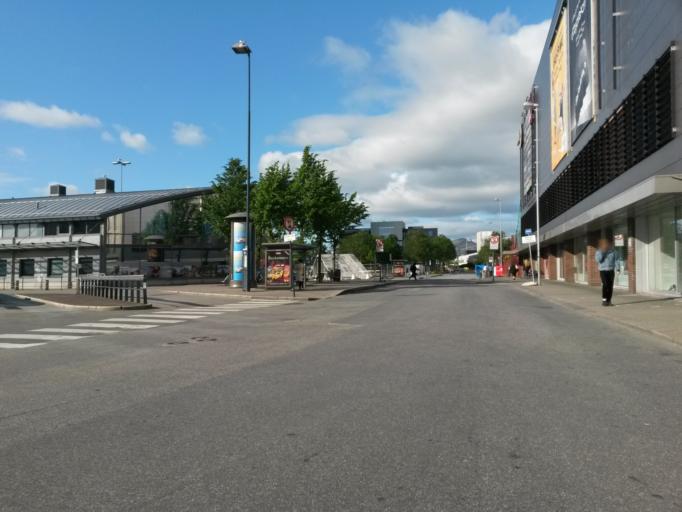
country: NO
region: Rogaland
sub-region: Sandnes
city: Sandnes
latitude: 58.8512
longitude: 5.7372
